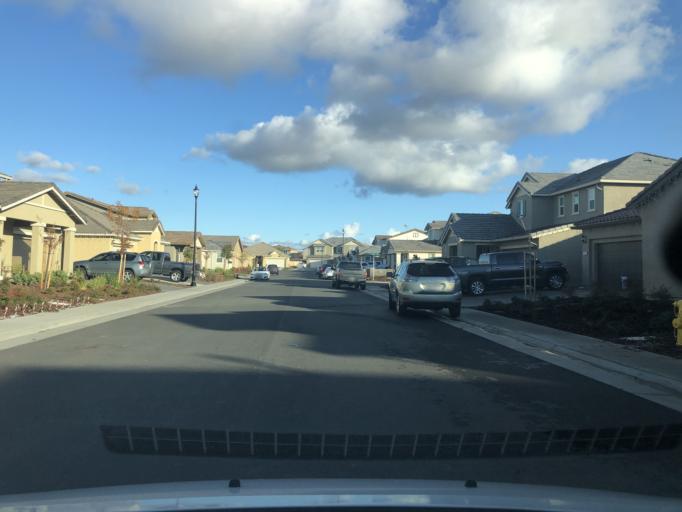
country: US
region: California
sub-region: Sacramento County
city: Antelope
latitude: 38.7697
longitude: -121.3791
